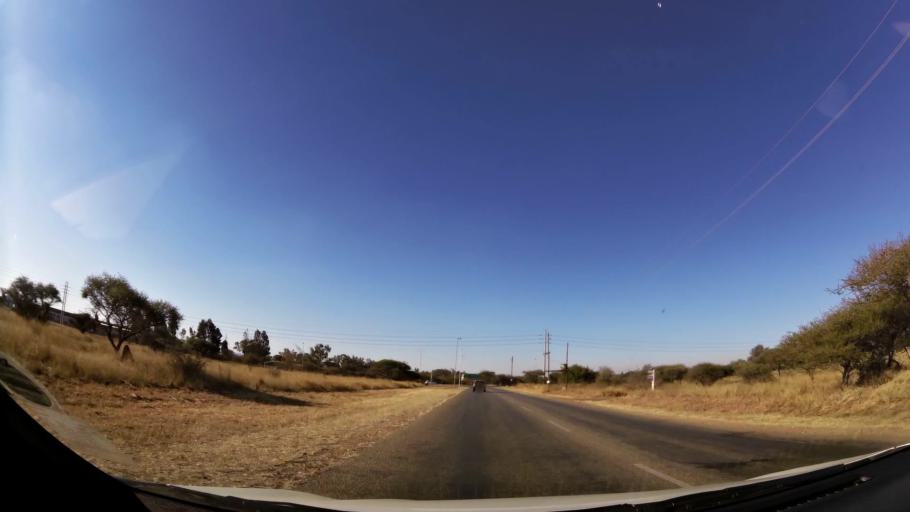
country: ZA
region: Limpopo
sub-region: Capricorn District Municipality
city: Polokwane
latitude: -23.8717
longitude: 29.4834
